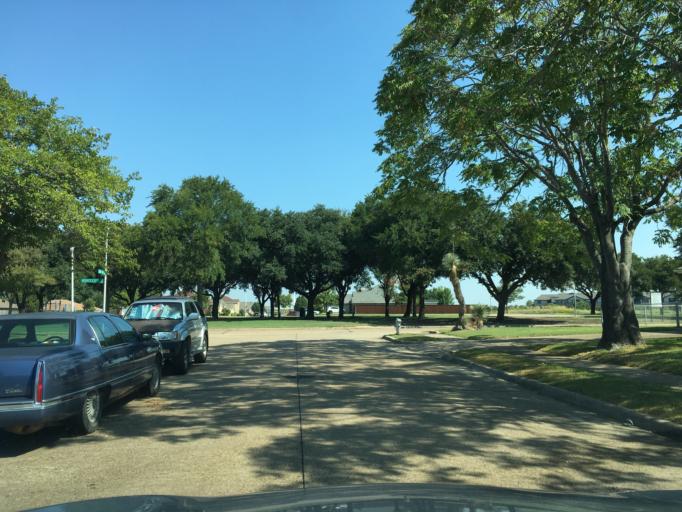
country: US
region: Texas
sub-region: Dallas County
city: Garland
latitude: 32.9331
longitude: -96.6347
